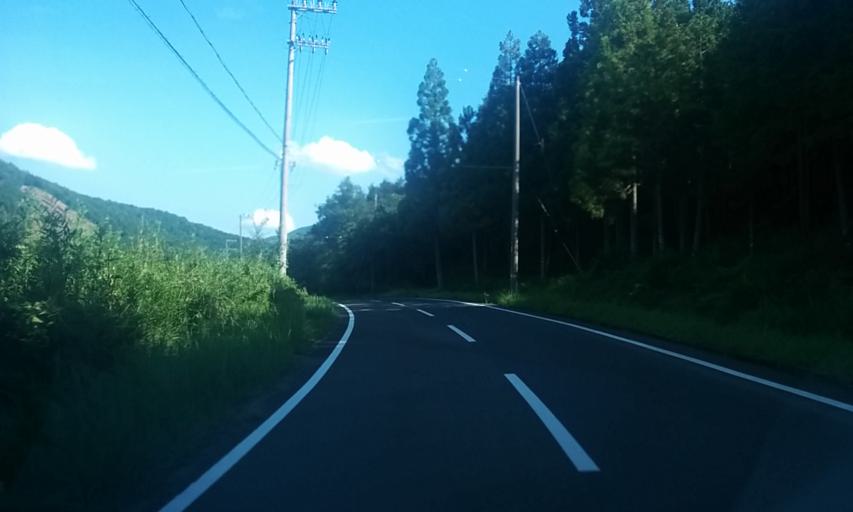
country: JP
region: Kyoto
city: Ayabe
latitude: 35.2887
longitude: 135.3286
